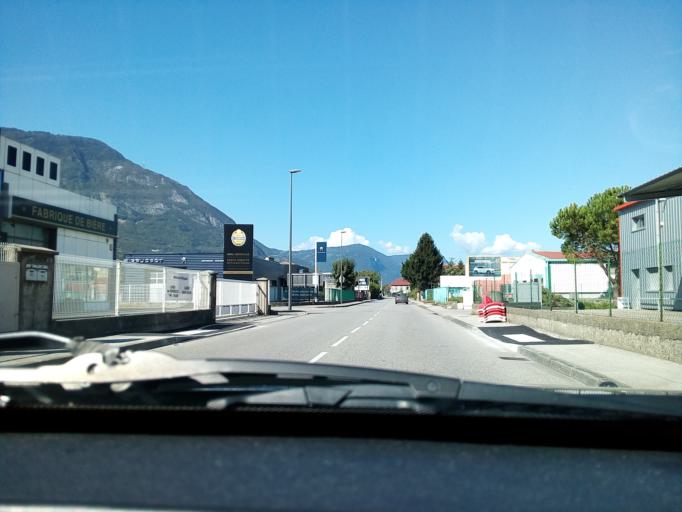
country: FR
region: Rhone-Alpes
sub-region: Departement de l'Isere
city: Fontaine
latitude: 45.2062
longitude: 5.6816
